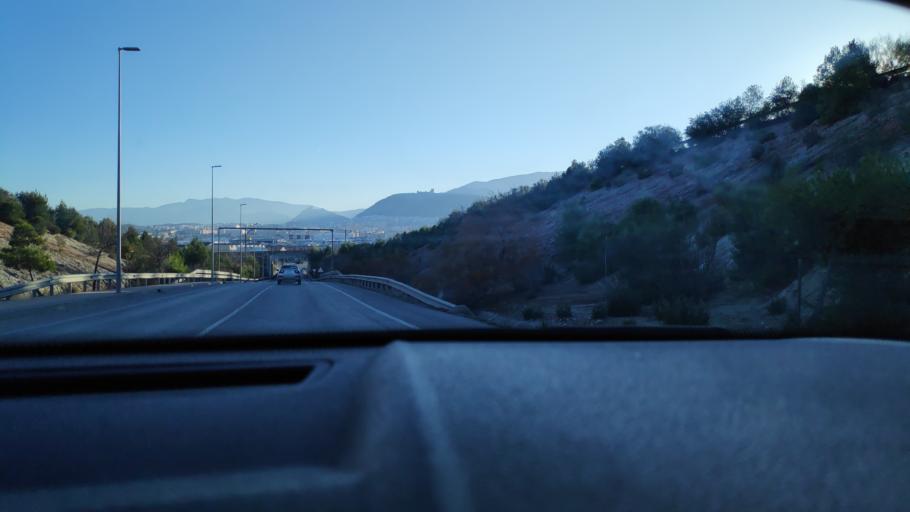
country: ES
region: Andalusia
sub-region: Provincia de Jaen
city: Jaen
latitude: 37.8057
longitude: -3.7881
